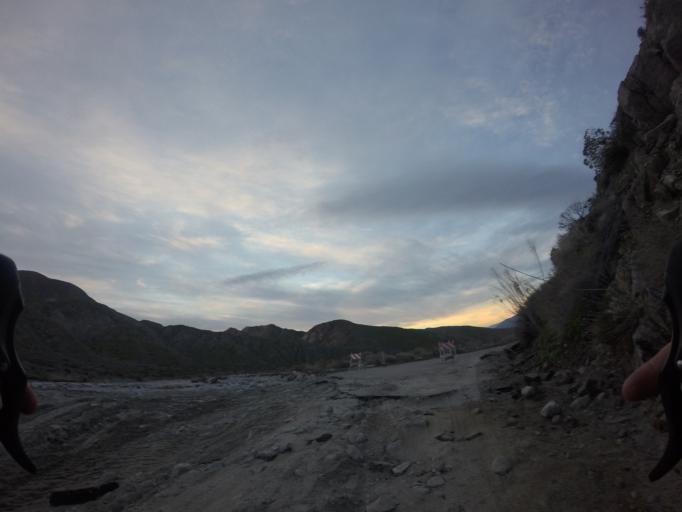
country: US
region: California
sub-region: San Bernardino County
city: Morongo Valley
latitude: 33.9575
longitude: -116.6456
